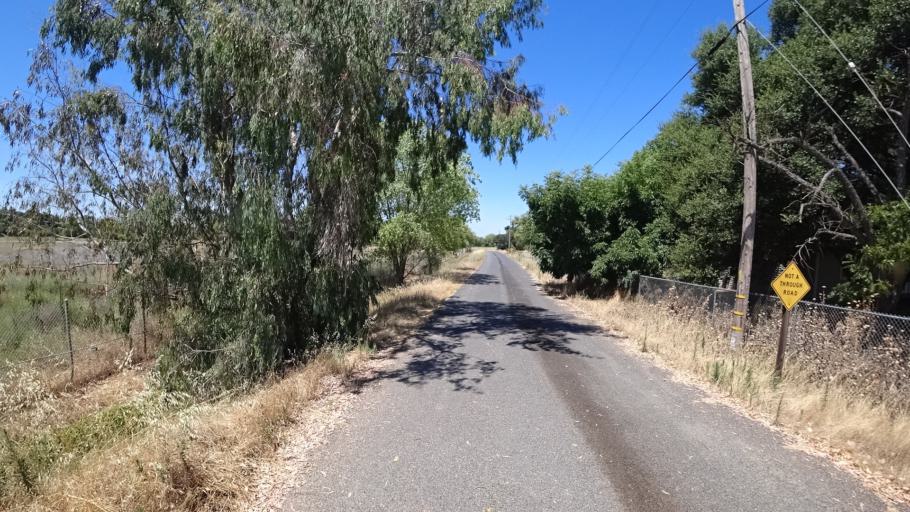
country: US
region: California
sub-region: San Joaquin County
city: Dogtown
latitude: 38.1957
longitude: -120.9799
